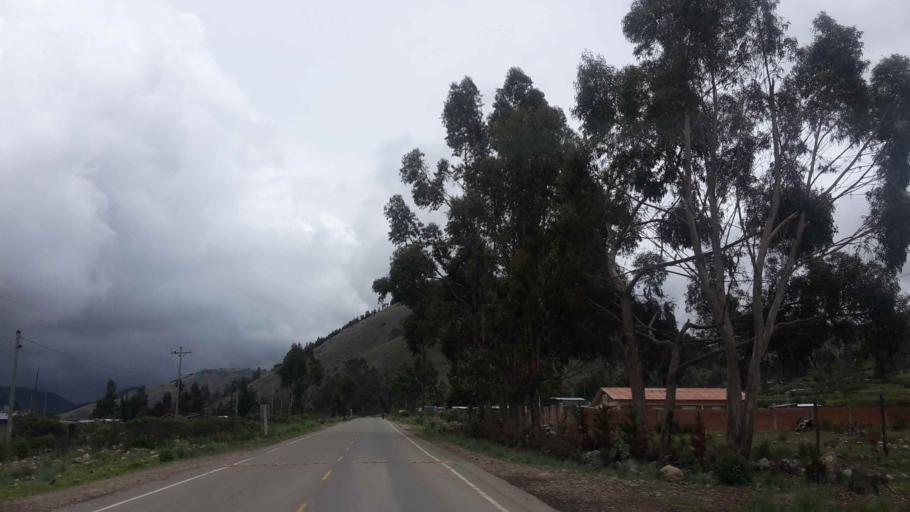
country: BO
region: Cochabamba
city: Arani
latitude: -17.4768
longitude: -65.5225
